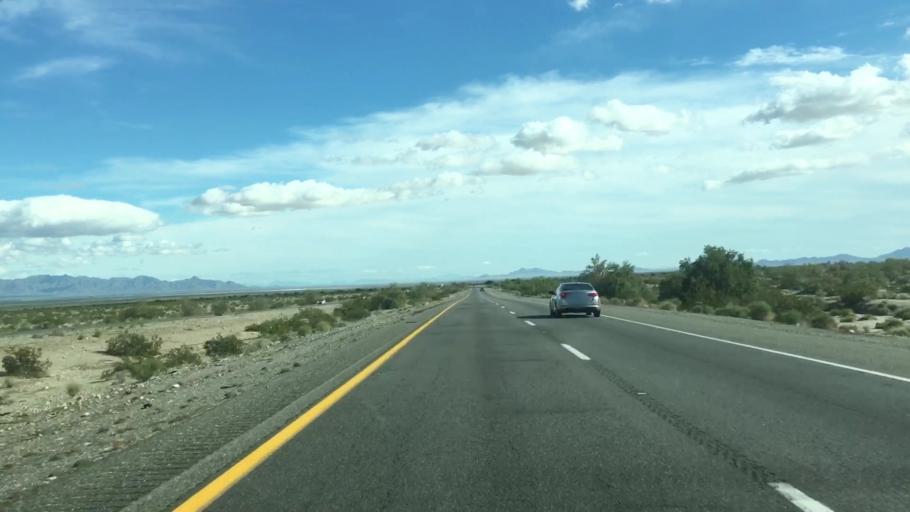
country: US
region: California
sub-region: Riverside County
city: Mesa Verde
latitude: 33.6618
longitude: -115.1749
